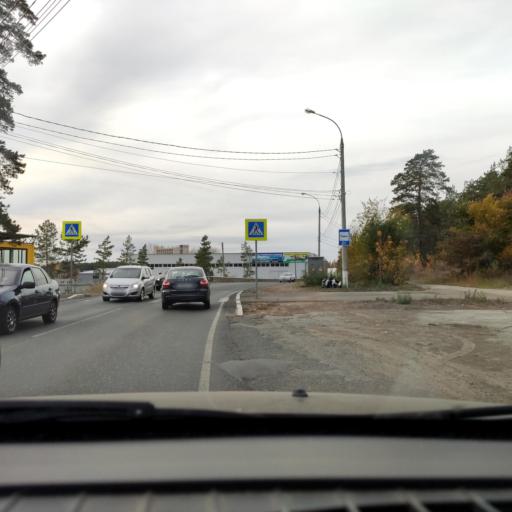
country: RU
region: Samara
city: Tol'yatti
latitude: 53.4761
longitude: 49.3273
